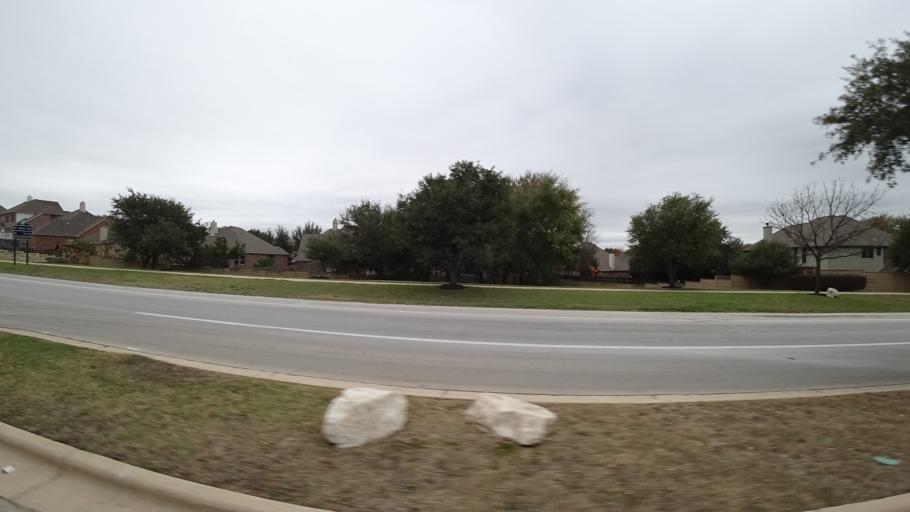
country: US
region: Texas
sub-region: Williamson County
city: Cedar Park
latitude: 30.4728
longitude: -97.8492
